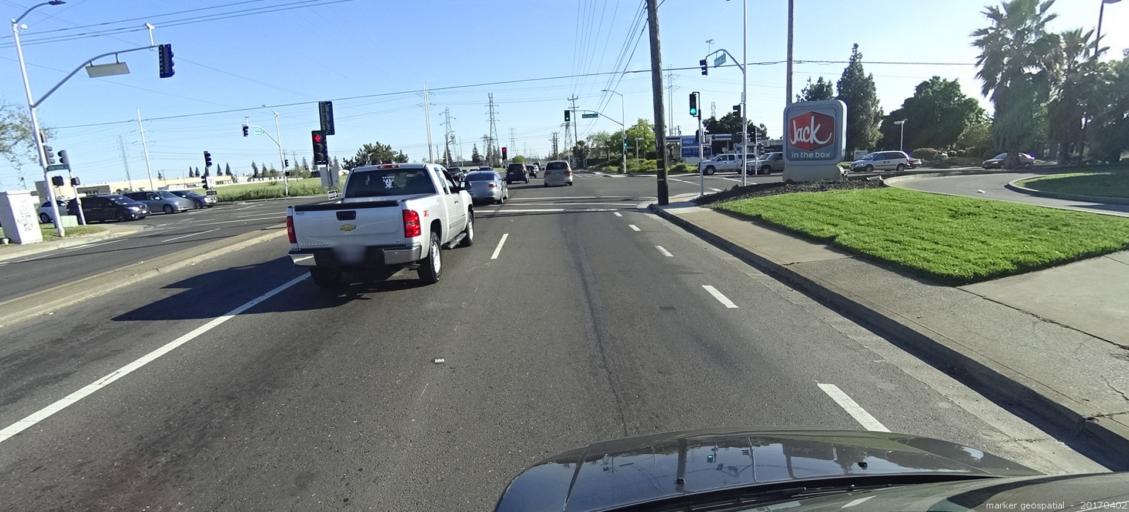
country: US
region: California
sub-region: Sacramento County
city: Florin
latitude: 38.5109
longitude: -121.4092
